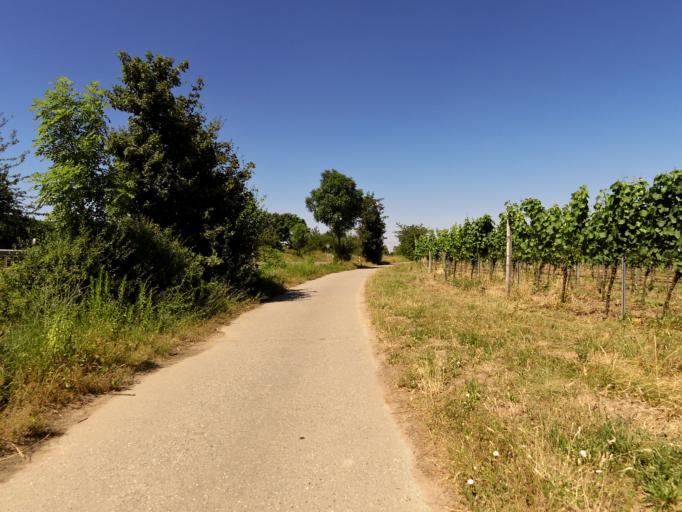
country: DE
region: Rheinland-Pfalz
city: Deidesheim
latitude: 49.3831
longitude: 8.1754
